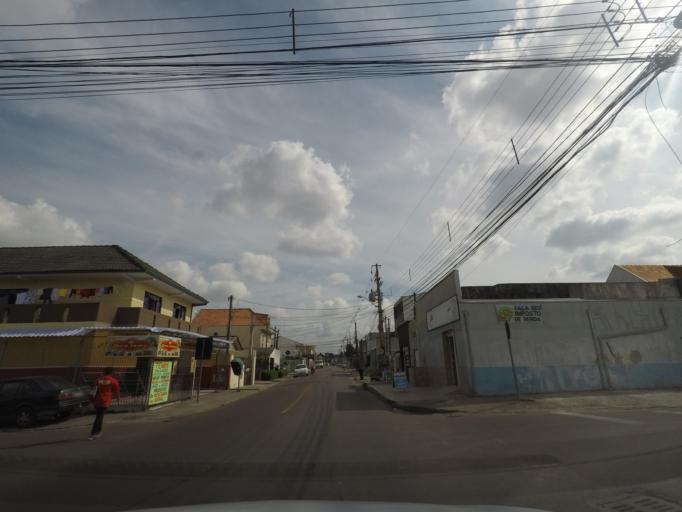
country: BR
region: Parana
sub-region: Sao Jose Dos Pinhais
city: Sao Jose dos Pinhais
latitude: -25.4909
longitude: -49.2034
